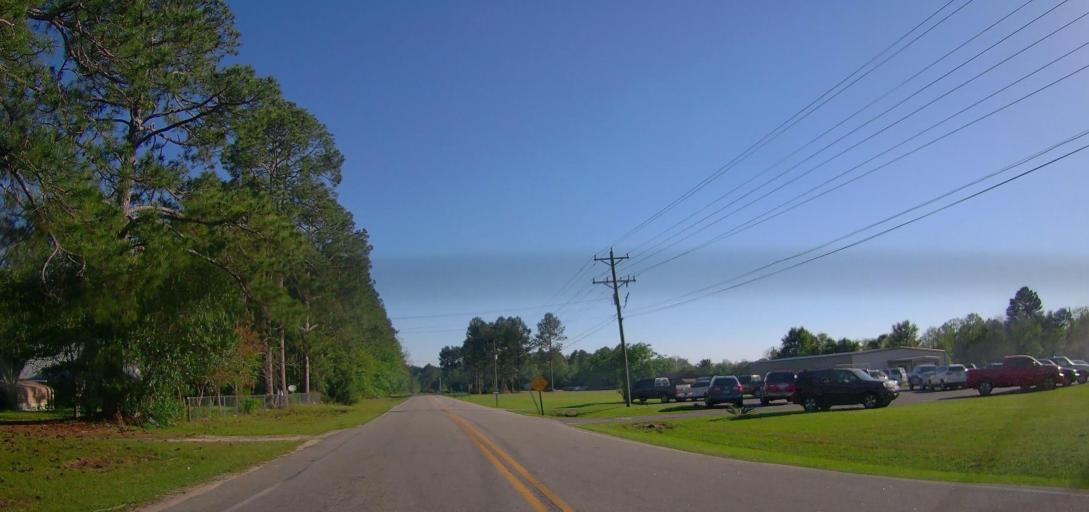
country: US
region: Georgia
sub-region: Ben Hill County
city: Fitzgerald
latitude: 31.7430
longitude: -83.2346
